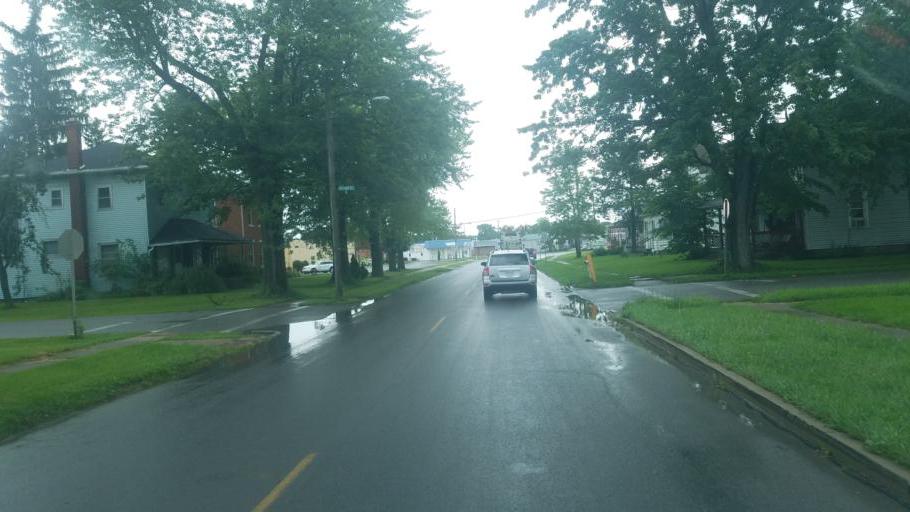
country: US
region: Ohio
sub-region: Hardin County
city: Kenton
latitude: 40.6405
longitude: -83.6071
